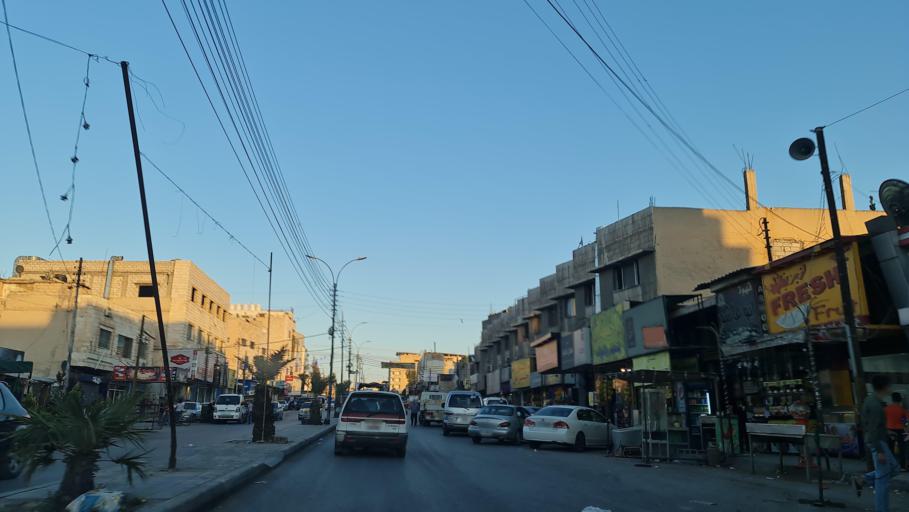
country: JO
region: Zarqa
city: Zarqa
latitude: 32.0767
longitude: 36.0763
